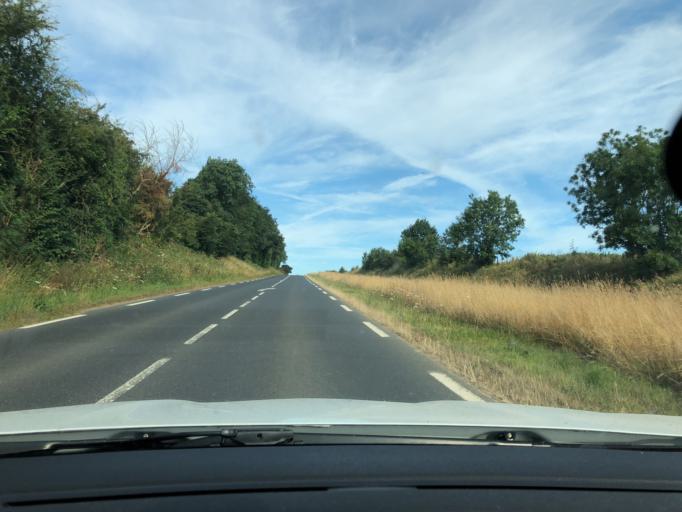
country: FR
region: Lower Normandy
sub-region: Departement du Calvados
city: Saint-Vigor-le-Grand
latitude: 49.2530
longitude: -0.6372
